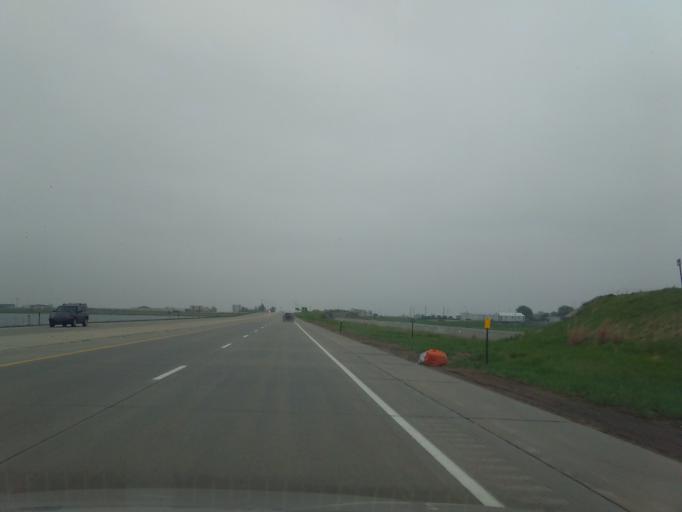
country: US
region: Nebraska
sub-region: Saunders County
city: Wahoo
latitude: 41.2348
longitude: -96.6126
